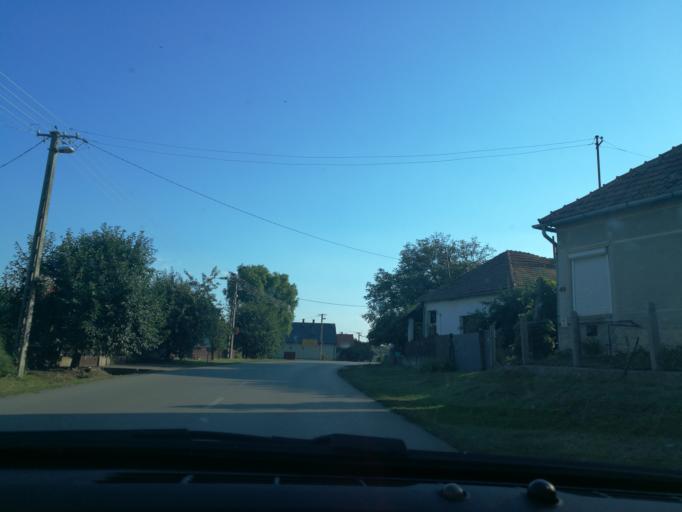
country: HU
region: Szabolcs-Szatmar-Bereg
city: Buj
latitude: 48.0974
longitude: 21.6457
